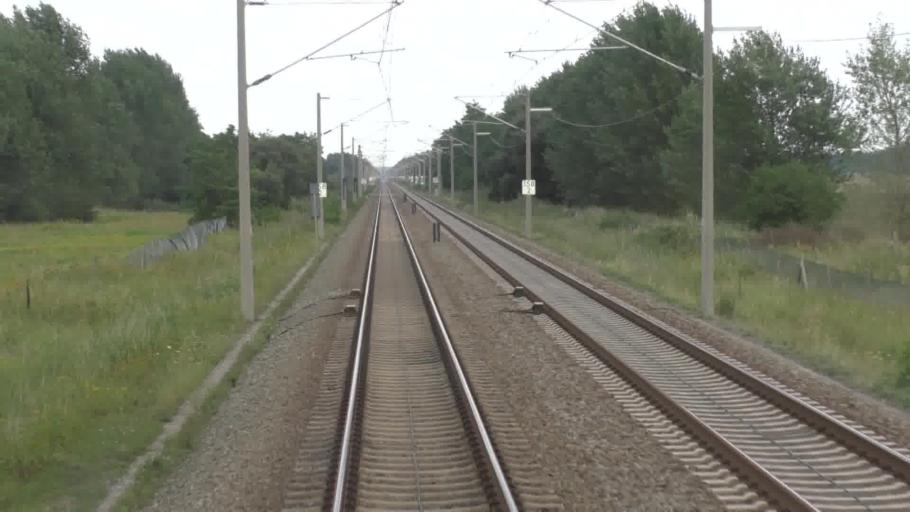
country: DE
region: Brandenburg
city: Nennhausen
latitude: 52.5977
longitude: 12.5395
